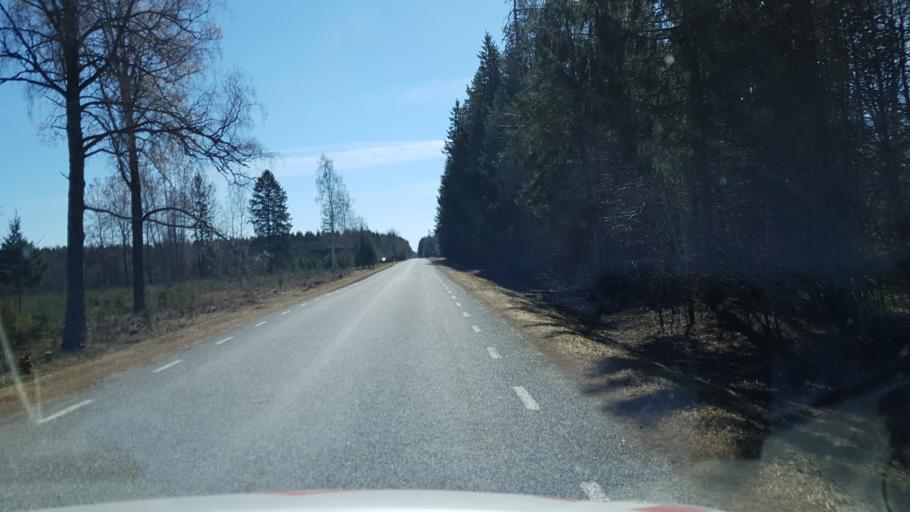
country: EE
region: Laeaene-Virumaa
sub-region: Vinni vald
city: Vinni
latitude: 59.1637
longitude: 26.5112
